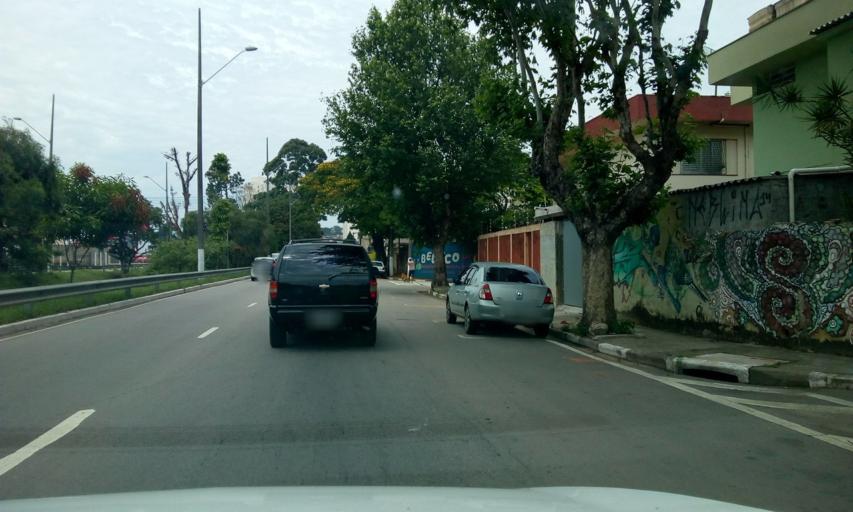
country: BR
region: Sao Paulo
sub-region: Jundiai
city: Jundiai
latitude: -23.2139
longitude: -46.8746
